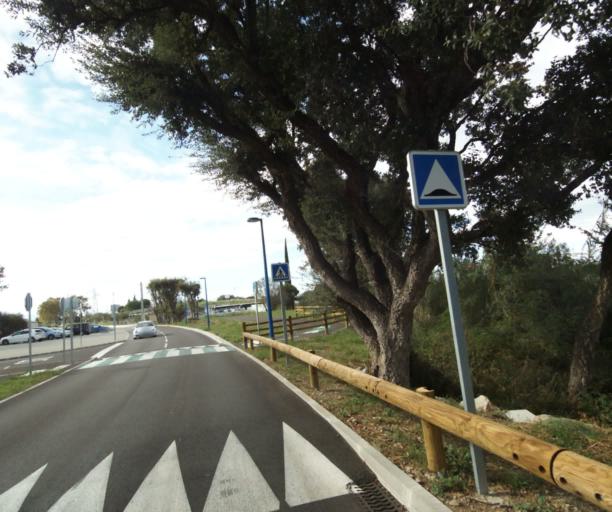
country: FR
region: Languedoc-Roussillon
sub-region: Departement des Pyrenees-Orientales
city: Argelers
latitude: 42.5501
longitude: 3.0106
